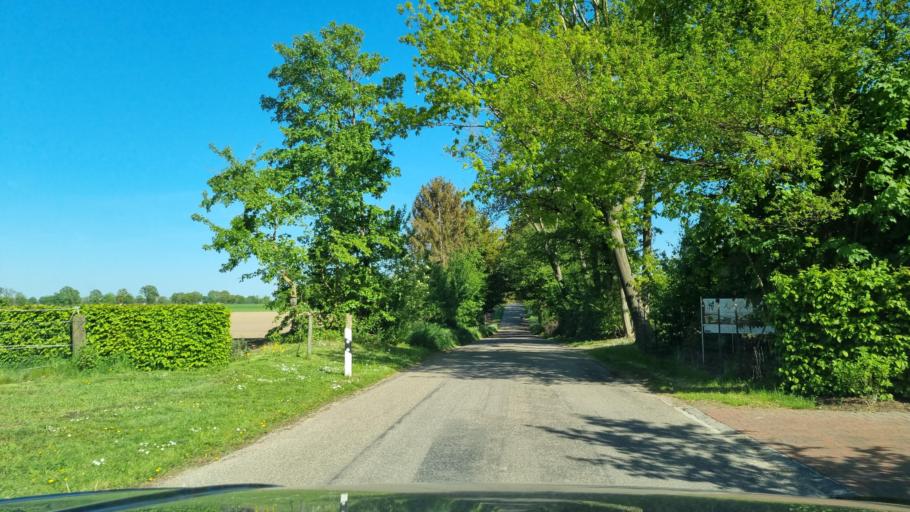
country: DE
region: North Rhine-Westphalia
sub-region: Regierungsbezirk Dusseldorf
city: Kleve
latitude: 51.7504
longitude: 6.1117
